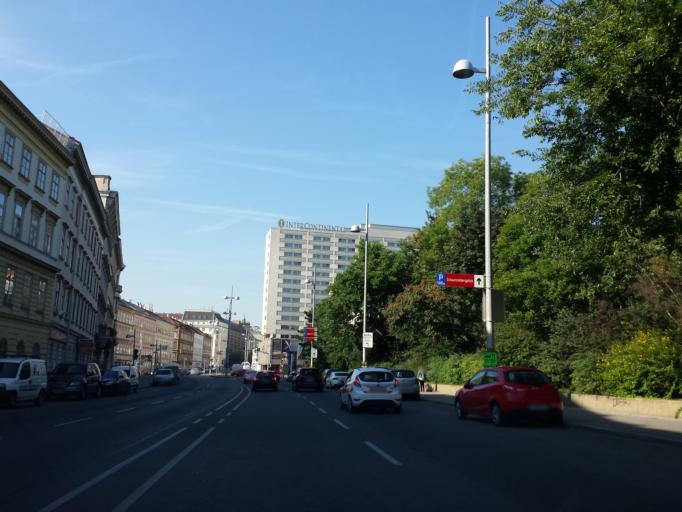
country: AT
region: Vienna
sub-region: Wien Stadt
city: Vienna
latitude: 48.2028
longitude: 16.3812
